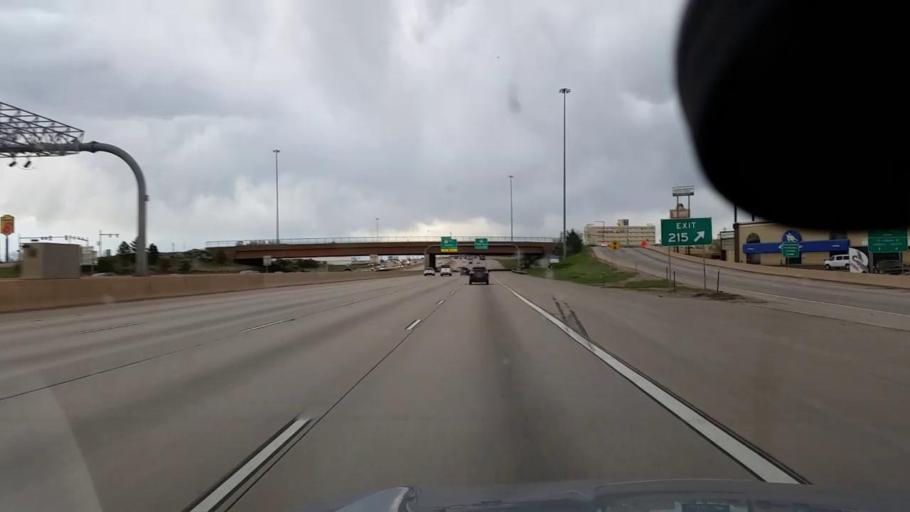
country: US
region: Colorado
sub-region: Adams County
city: Twin Lakes
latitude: 39.7999
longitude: -104.9854
